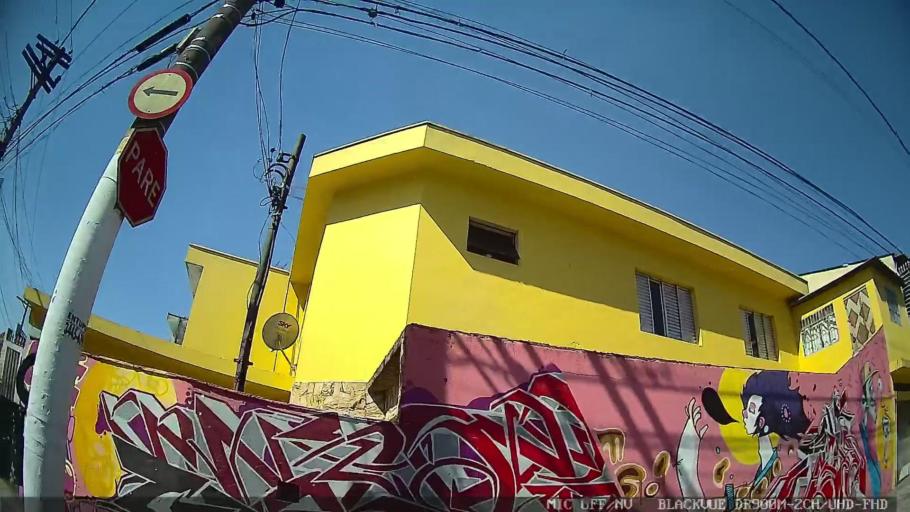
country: BR
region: Sao Paulo
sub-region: Sao Caetano Do Sul
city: Sao Caetano do Sul
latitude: -23.5838
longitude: -46.4978
